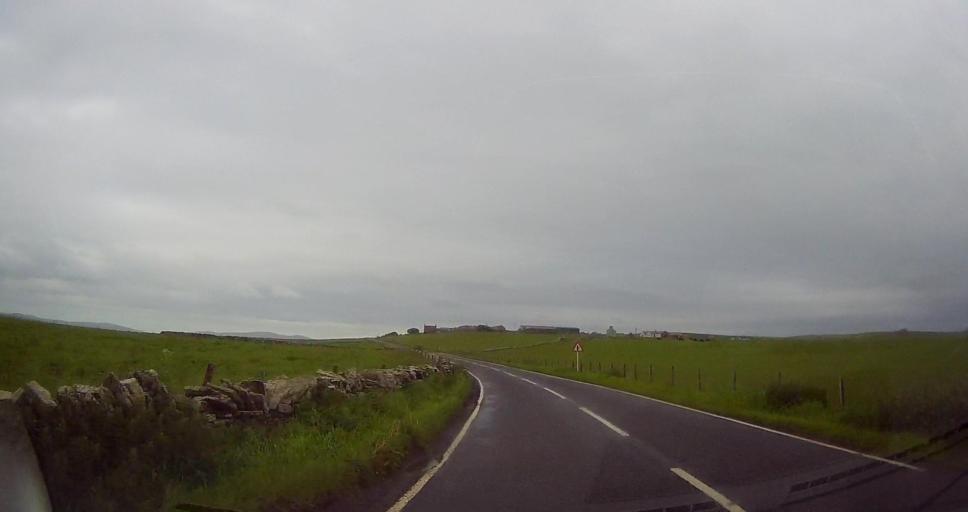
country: GB
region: Scotland
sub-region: Orkney Islands
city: Stromness
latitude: 59.0147
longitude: -3.3033
